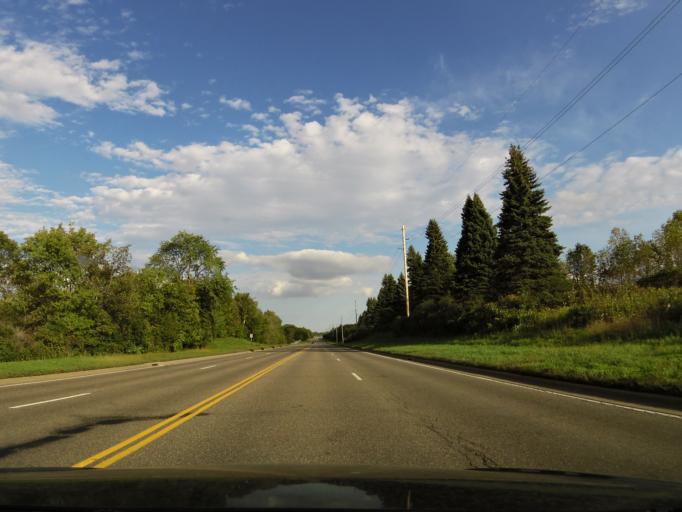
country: US
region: Minnesota
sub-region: Scott County
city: Prior Lake
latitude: 44.7011
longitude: -93.3955
